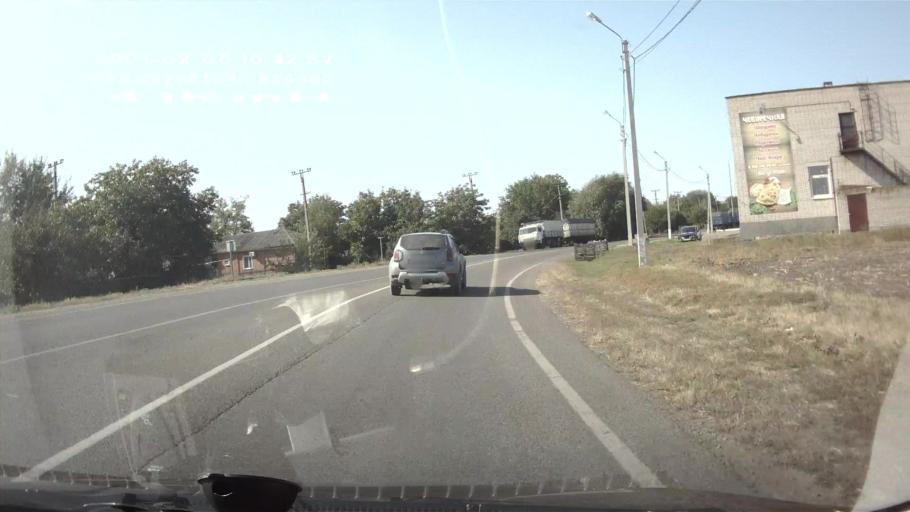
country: RU
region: Krasnodarskiy
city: Belaya Glina
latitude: 46.0973
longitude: 40.8516
